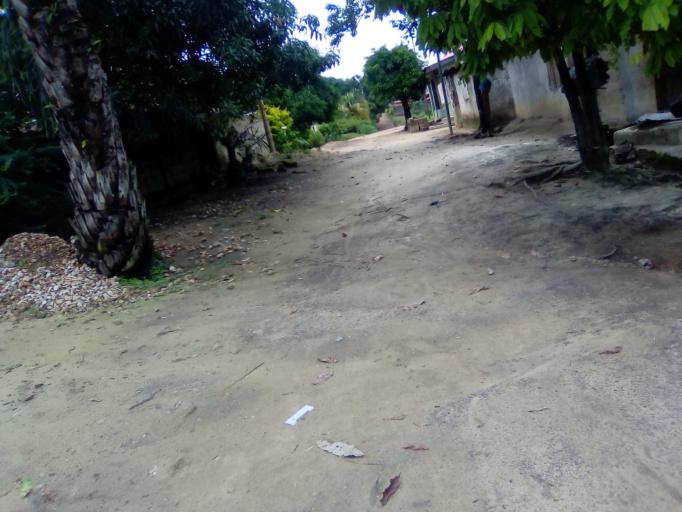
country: SL
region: Southern Province
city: Bo
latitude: 7.9463
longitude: -11.7118
